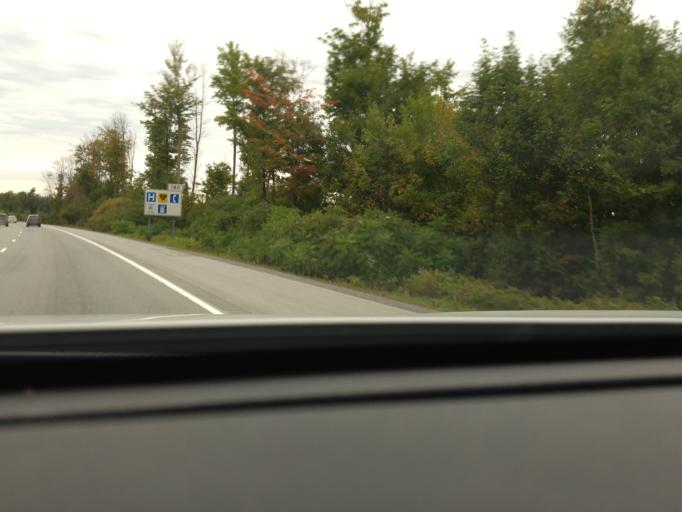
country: CA
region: Ontario
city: Arnprior
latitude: 45.4160
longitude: -76.3044
